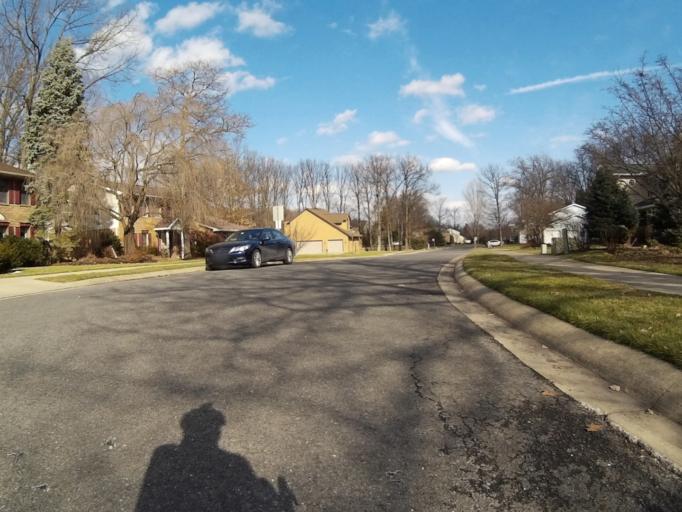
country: US
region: Pennsylvania
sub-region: Centre County
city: Park Forest Village
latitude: 40.7988
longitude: -77.9169
